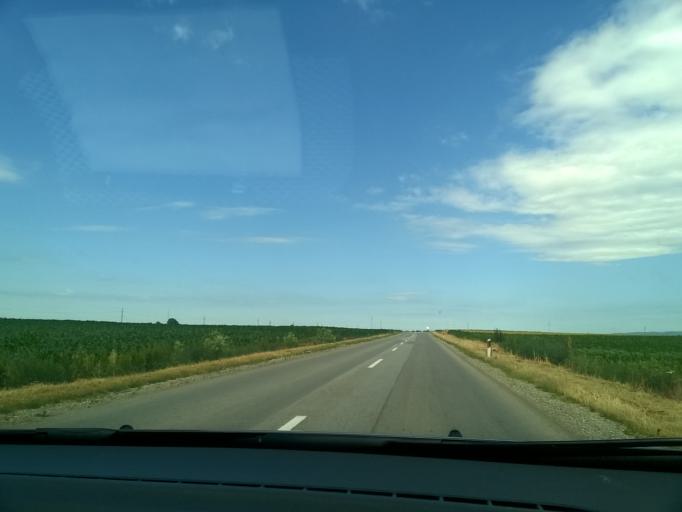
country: RS
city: Putinci
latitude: 45.0063
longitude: 19.9074
